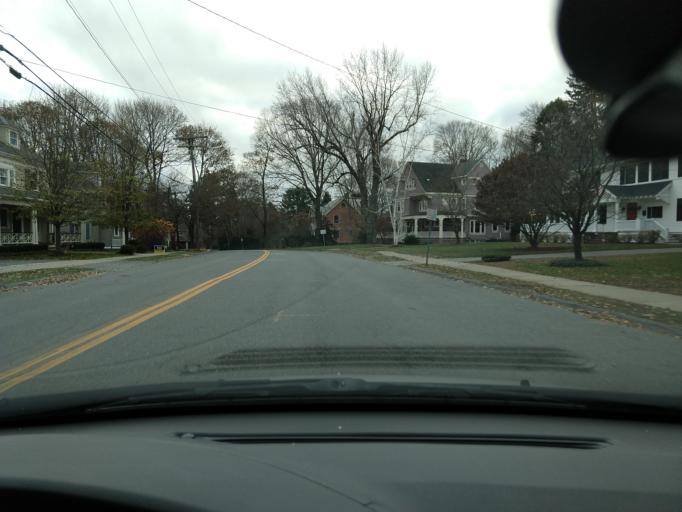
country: US
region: Massachusetts
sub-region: Middlesex County
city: Lexington
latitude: 42.4444
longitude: -71.2241
